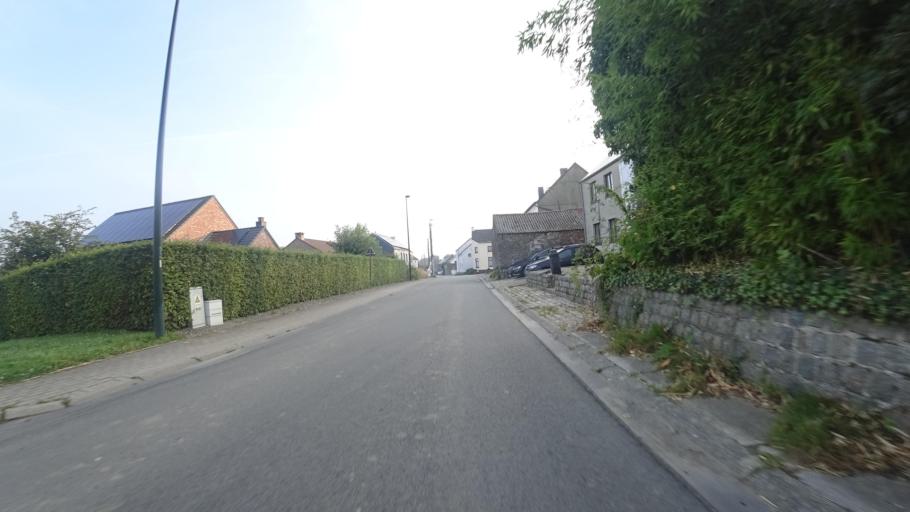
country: BE
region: Wallonia
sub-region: Province du Brabant Wallon
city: Walhain-Saint-Paul
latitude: 50.6259
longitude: 4.7230
